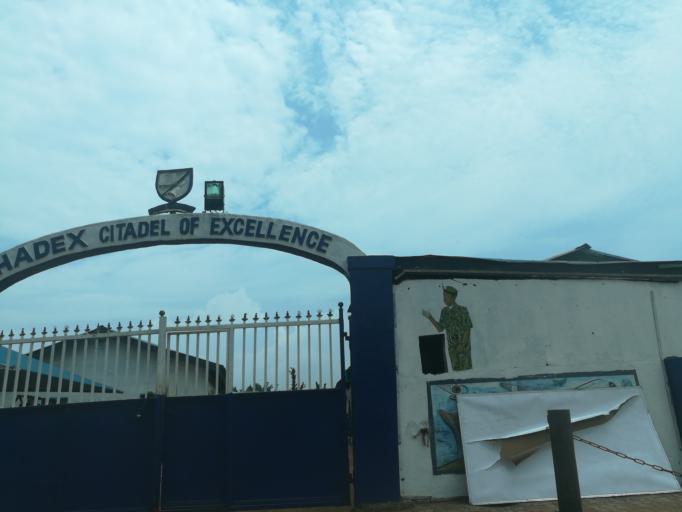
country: NG
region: Lagos
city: Ikorodu
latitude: 6.5821
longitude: 3.5907
